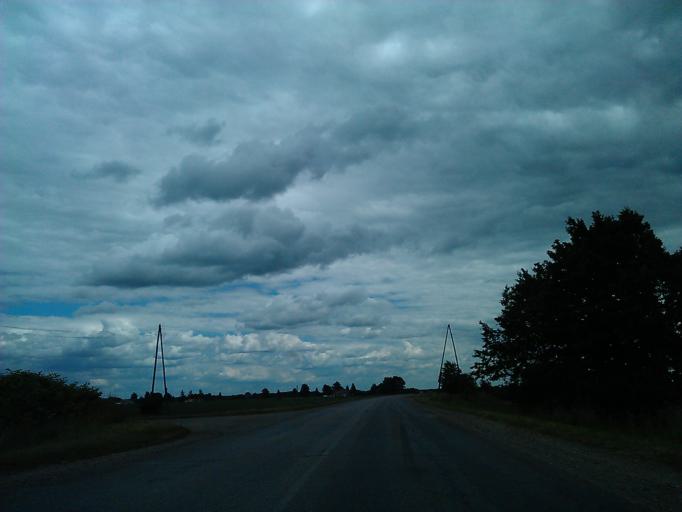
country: LV
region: Dobeles Rajons
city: Dobele
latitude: 56.6302
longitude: 23.3199
